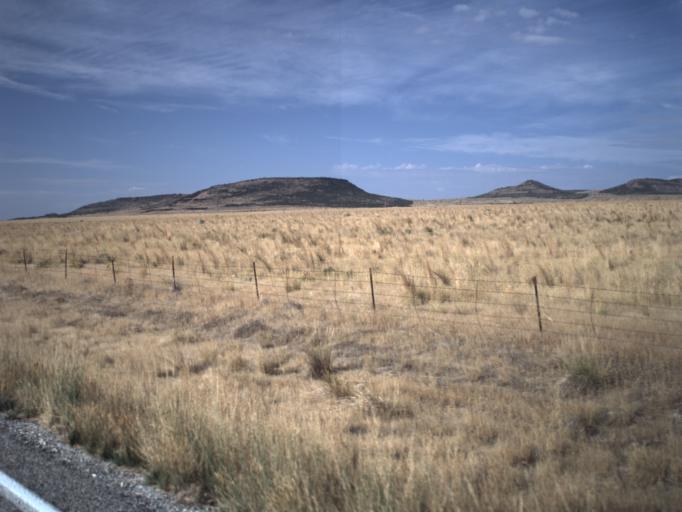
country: US
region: Idaho
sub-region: Oneida County
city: Malad City
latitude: 41.8741
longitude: -113.1212
